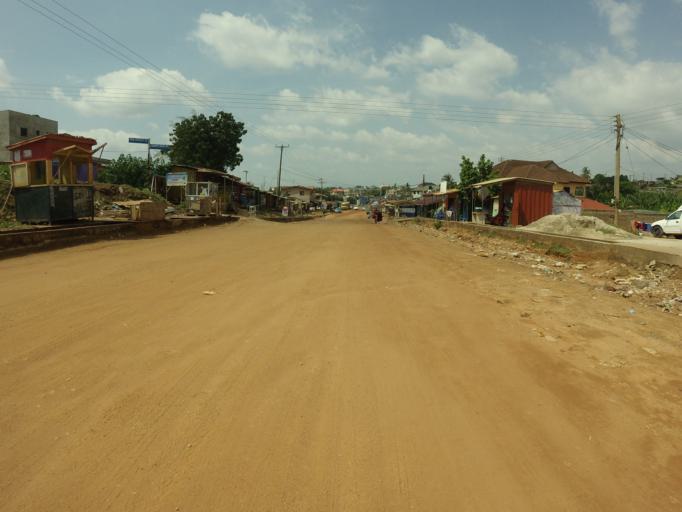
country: GH
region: Greater Accra
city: Gbawe
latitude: 5.6233
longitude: -0.3059
